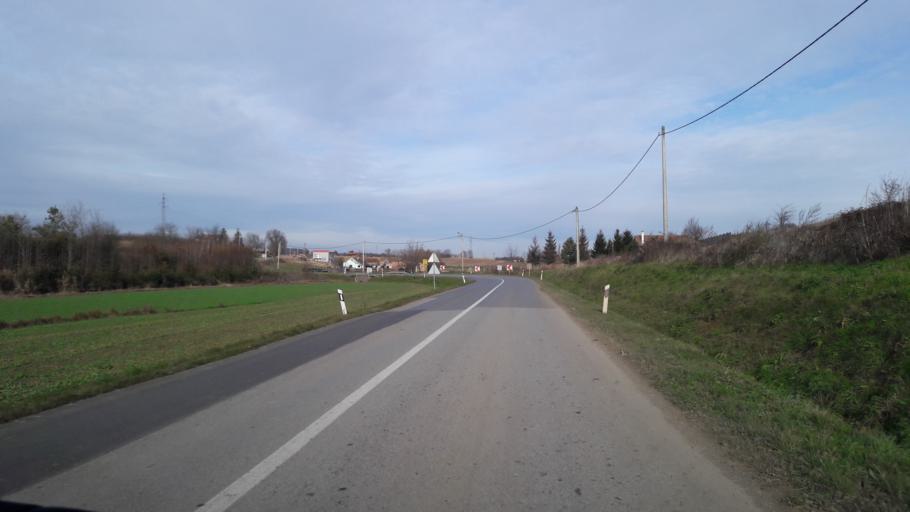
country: HR
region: Osjecko-Baranjska
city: Piskorevci
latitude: 45.2946
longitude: 18.4296
